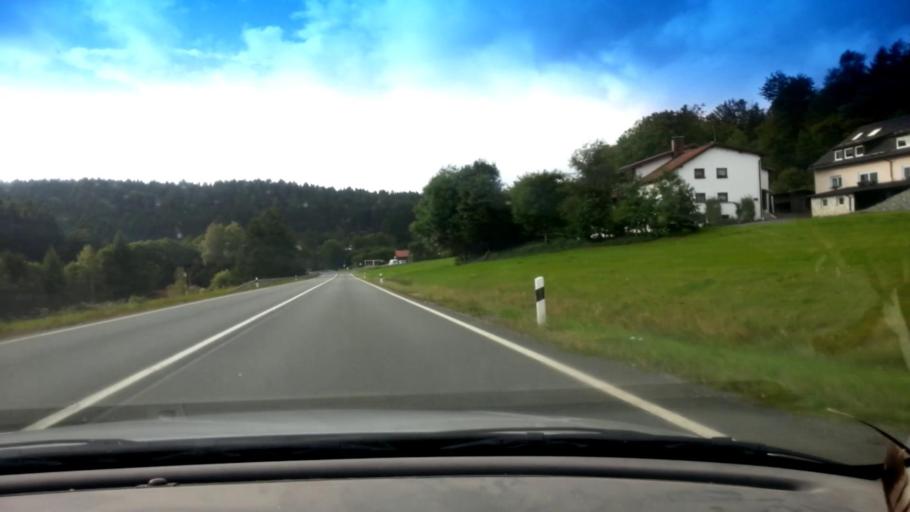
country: DE
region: Bavaria
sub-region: Upper Franconia
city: Bischofsgrun
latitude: 50.0594
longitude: 11.7908
